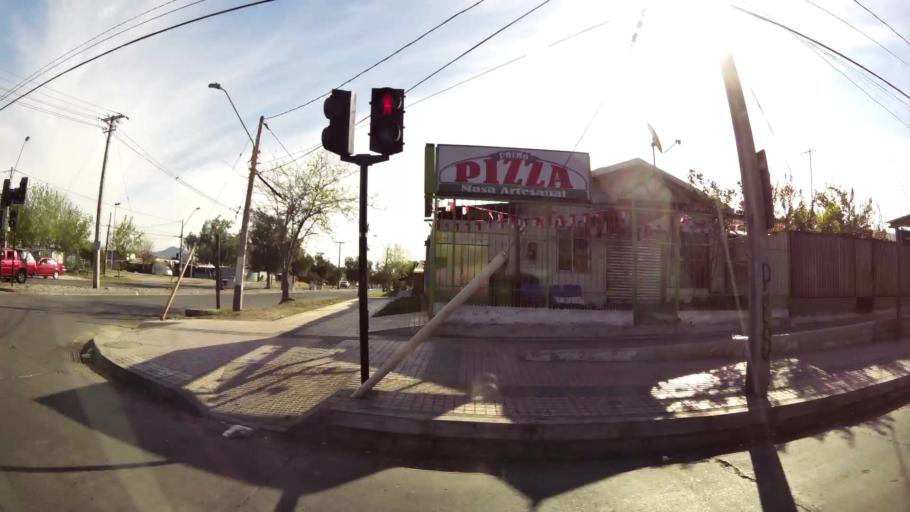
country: CL
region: Santiago Metropolitan
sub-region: Provincia de Cordillera
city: Puente Alto
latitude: -33.6186
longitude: -70.5908
